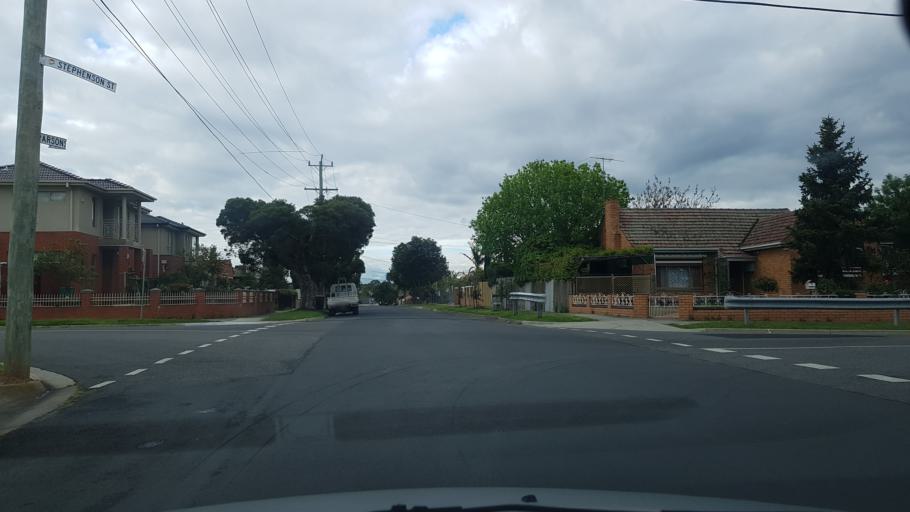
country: AU
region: Victoria
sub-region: Greater Dandenong
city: Springvale
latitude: -37.9419
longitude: 145.1518
